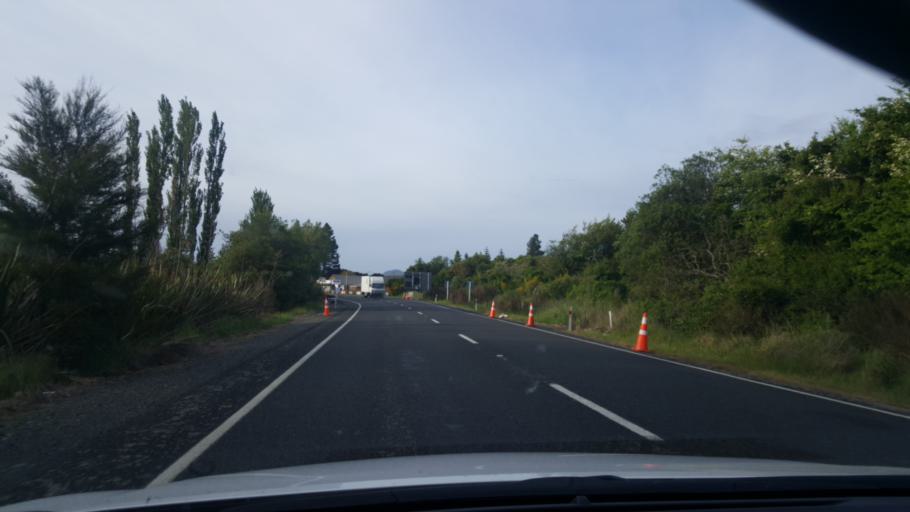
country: NZ
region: Waikato
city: Turangi
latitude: -38.9729
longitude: 175.7705
